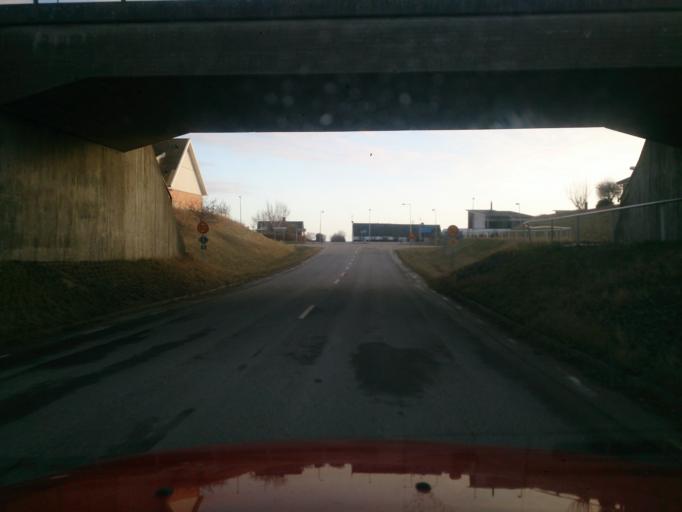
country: SE
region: Skane
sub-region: Ystads Kommun
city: Ystad
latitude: 55.4289
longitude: 13.7185
